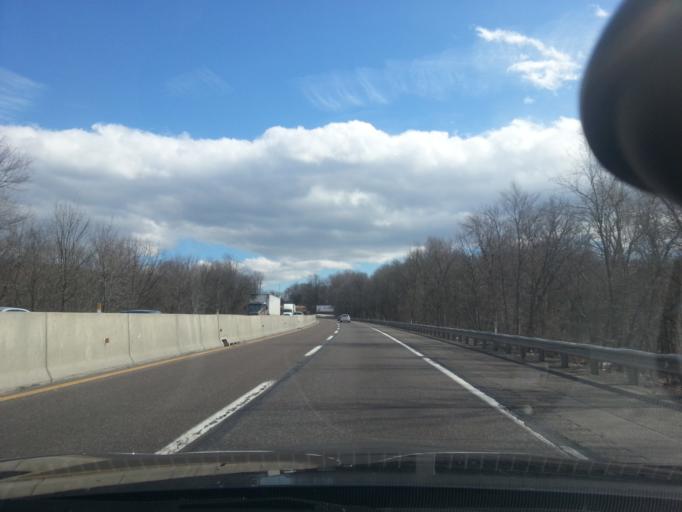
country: US
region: Pennsylvania
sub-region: Lehigh County
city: Emmaus
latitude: 40.5024
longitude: -75.4997
